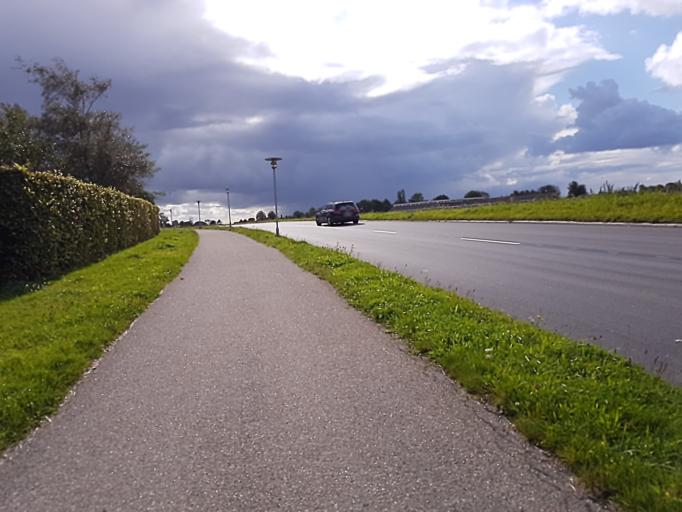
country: DK
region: Zealand
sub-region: Roskilde Kommune
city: Gundsomagle
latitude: 55.7369
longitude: 12.1401
